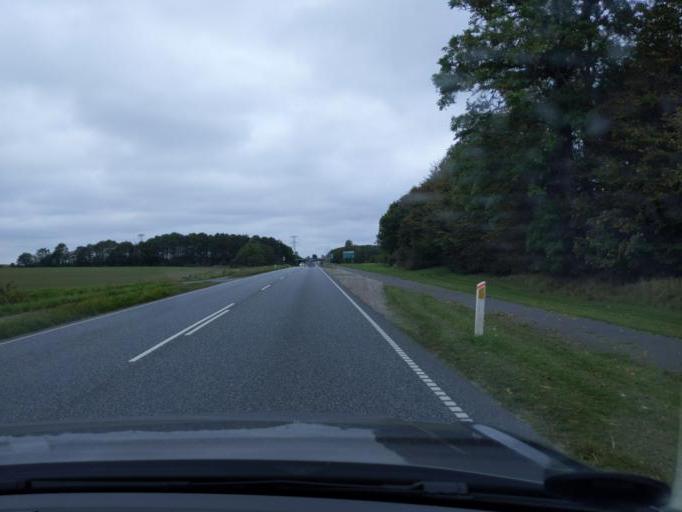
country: DK
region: Central Jutland
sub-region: Randers Kommune
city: Randers
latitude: 56.4887
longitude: 9.9849
